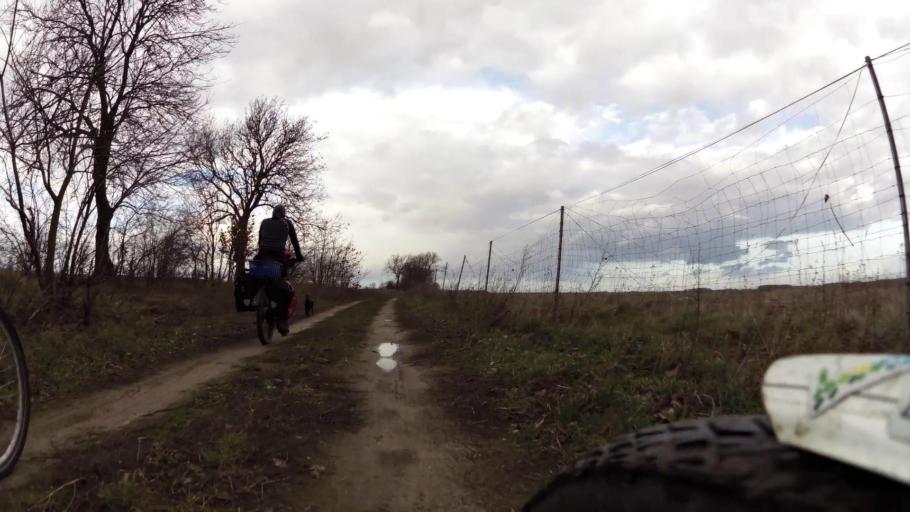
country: PL
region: West Pomeranian Voivodeship
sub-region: Powiat kamienski
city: Wolin
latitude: 53.8765
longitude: 14.7104
